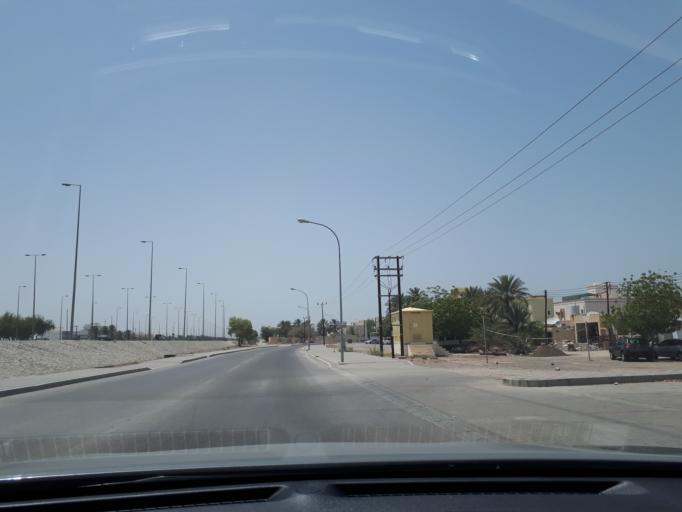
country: OM
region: Muhafazat Masqat
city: As Sib al Jadidah
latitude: 23.6775
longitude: 58.1311
